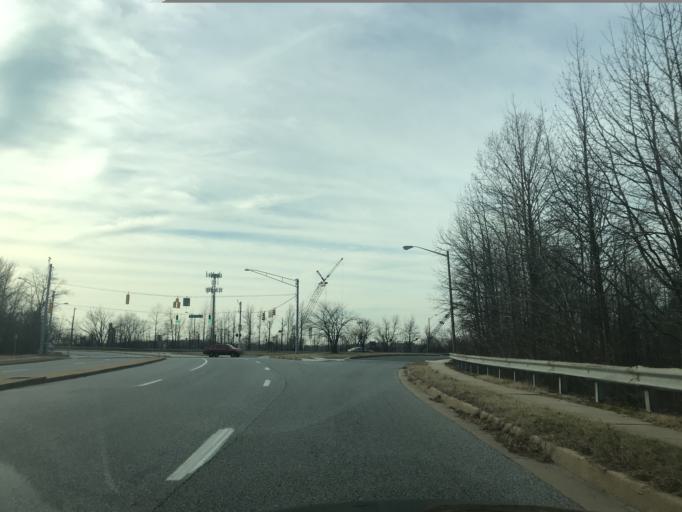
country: US
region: Maryland
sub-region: Baltimore County
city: Rossville
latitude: 39.3282
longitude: -76.4683
